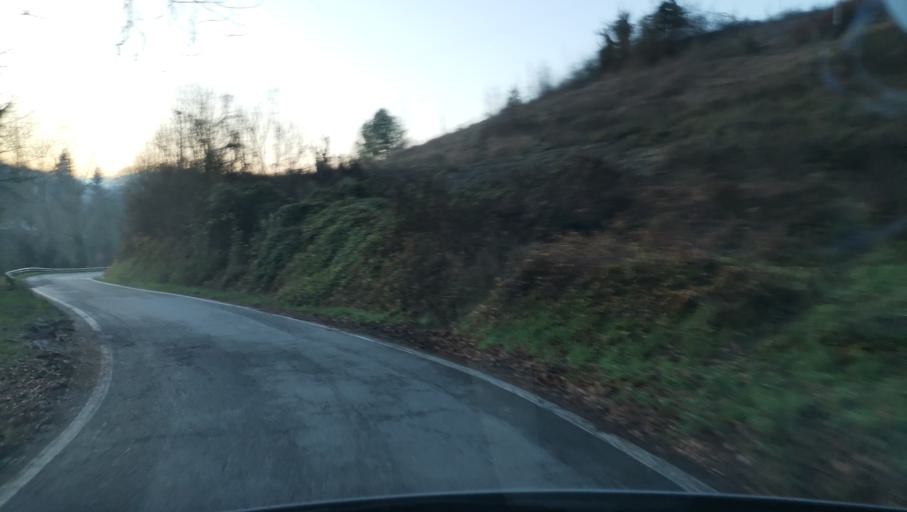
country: IT
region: Piedmont
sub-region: Provincia di Torino
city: Cinzano
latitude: 45.1082
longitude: 7.9160
